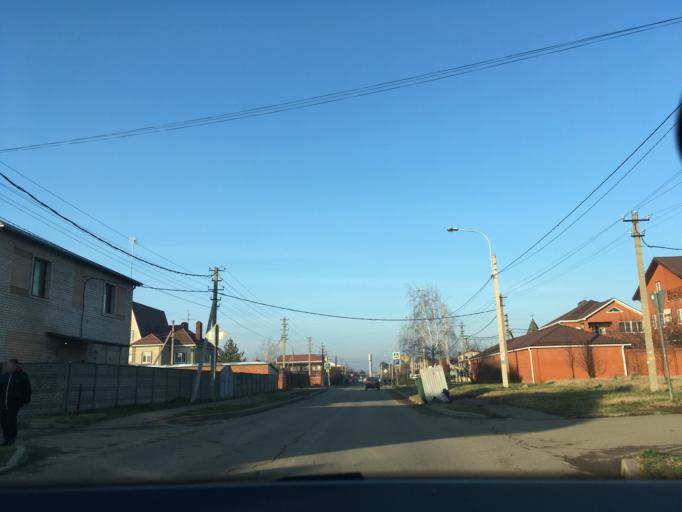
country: RU
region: Krasnodarskiy
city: Krasnodar
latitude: 45.1217
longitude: 39.0142
